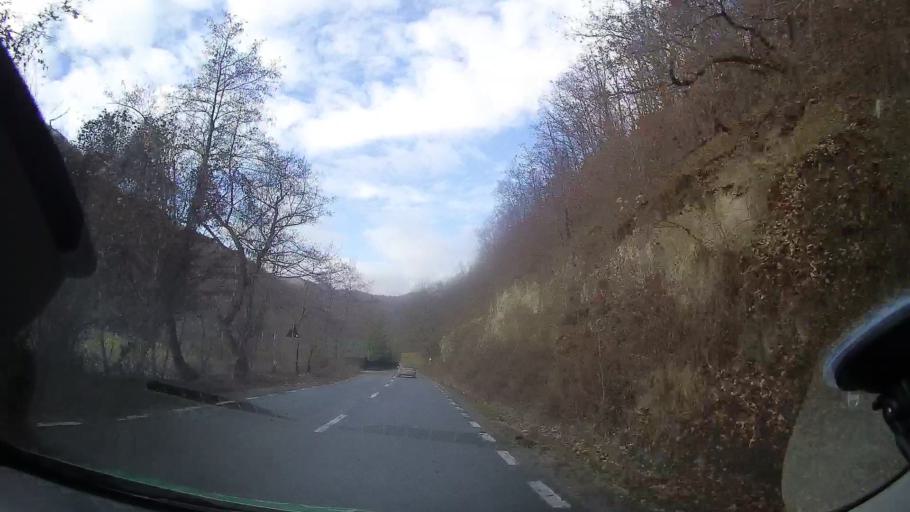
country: RO
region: Cluj
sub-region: Comuna Baisoara
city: Baisoara
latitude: 46.6096
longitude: 23.4167
